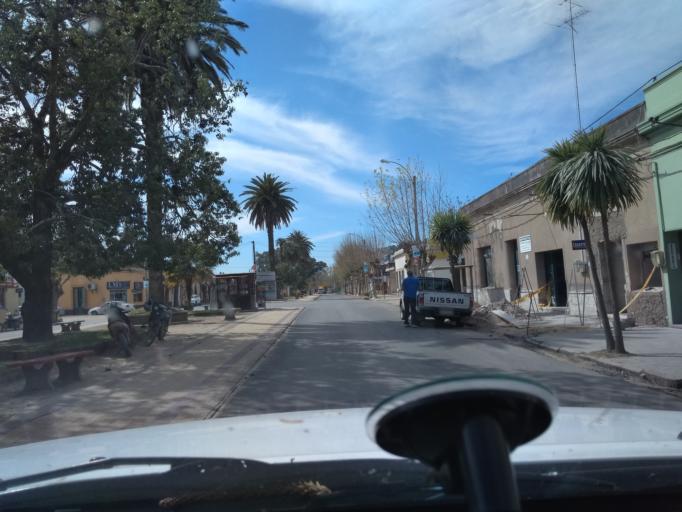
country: UY
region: Canelones
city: San Ramon
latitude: -34.2855
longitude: -55.9570
